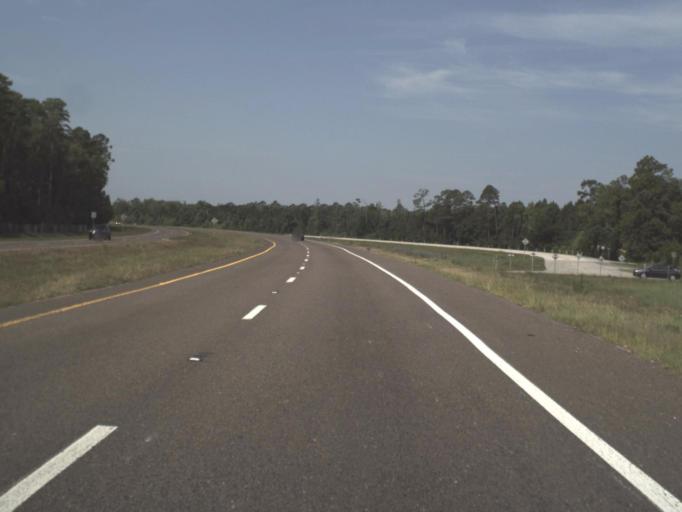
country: US
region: Florida
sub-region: Saint Johns County
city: Saint Augustine Shores
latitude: 29.8050
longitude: -81.4084
